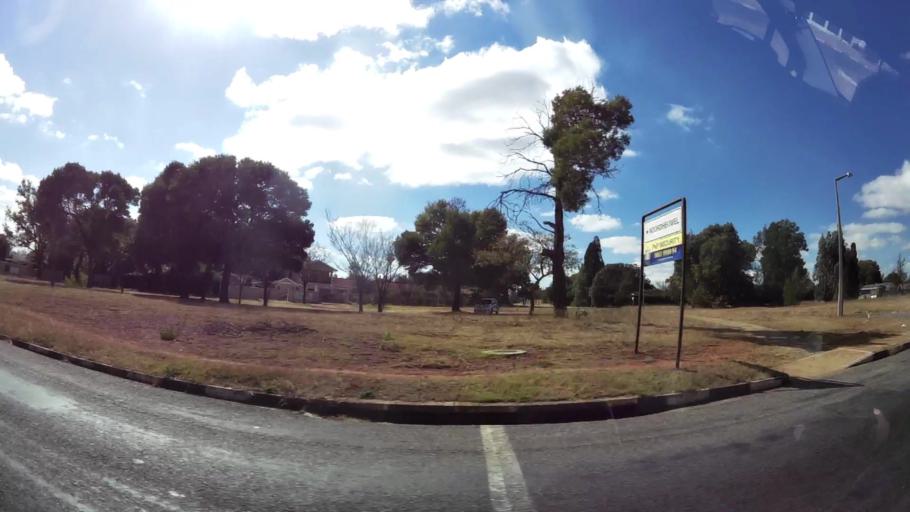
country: ZA
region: Gauteng
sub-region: West Rand District Municipality
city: Krugersdorp
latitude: -26.0946
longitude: 27.7908
